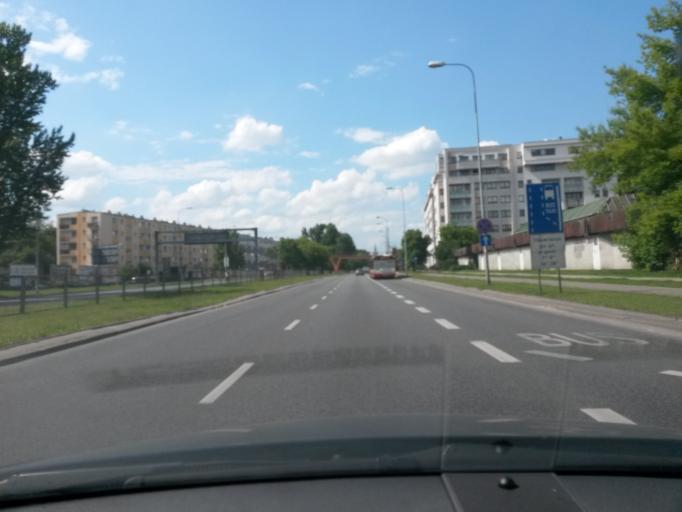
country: PL
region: Masovian Voivodeship
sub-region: Warszawa
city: Mokotow
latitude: 52.1964
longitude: 21.0406
